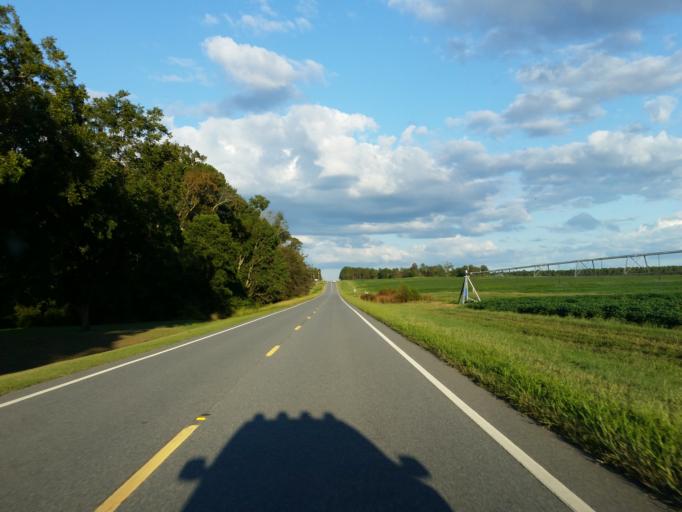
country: US
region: Georgia
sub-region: Dooly County
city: Vienna
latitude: 32.0863
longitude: -83.7362
